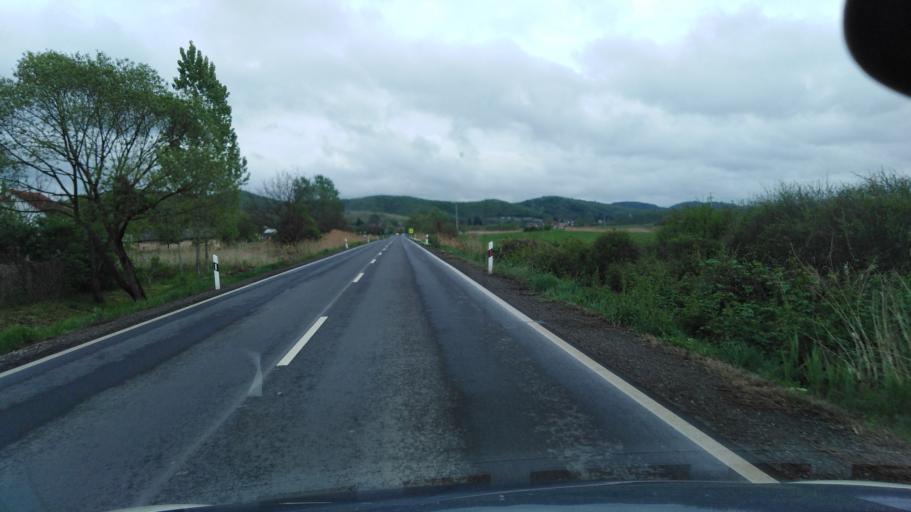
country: HU
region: Nograd
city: Karancskeszi
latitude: 48.1136
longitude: 19.6599
